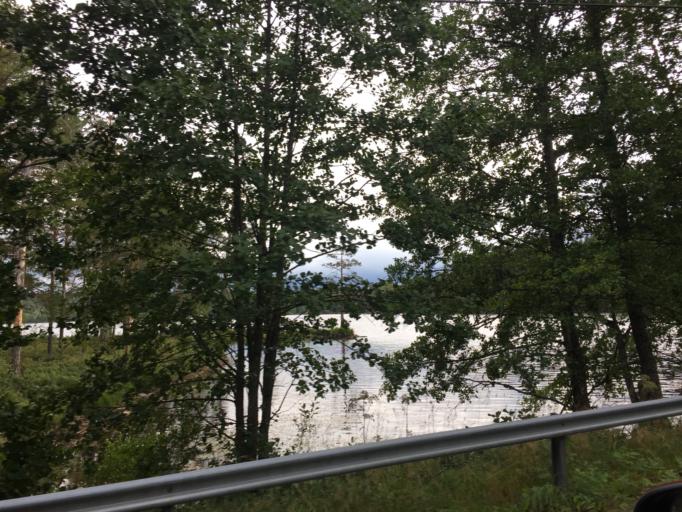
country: SE
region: Vaermland
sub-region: Filipstads Kommun
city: Lesjofors
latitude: 60.0322
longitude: 14.1144
